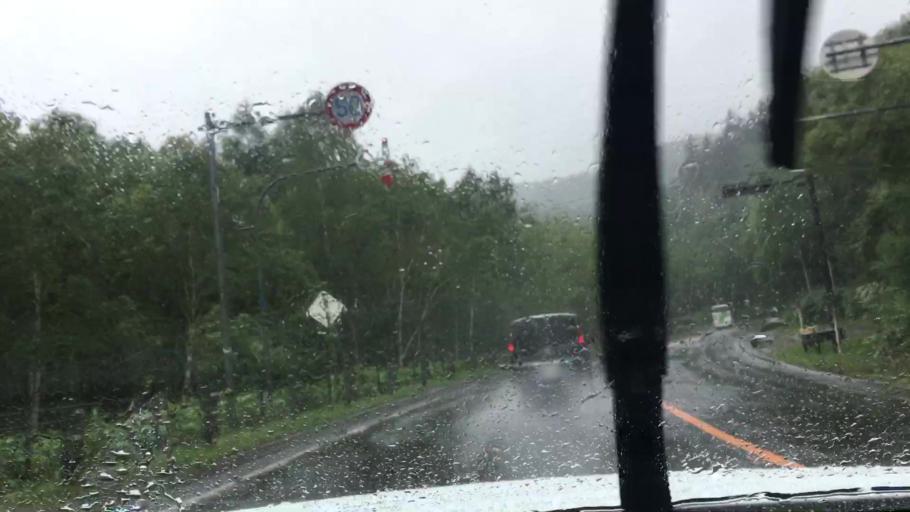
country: JP
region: Hokkaido
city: Sapporo
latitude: 42.8855
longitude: 141.1415
